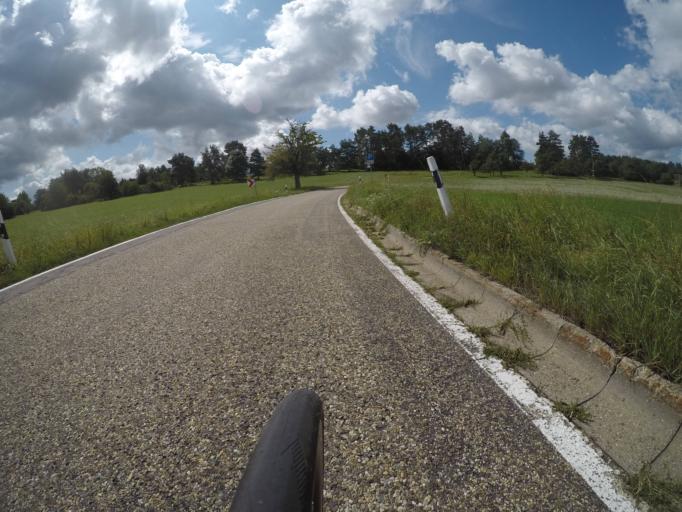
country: DE
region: Baden-Wuerttemberg
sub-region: Karlsruhe Region
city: Gechingen
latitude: 48.6734
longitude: 8.8560
